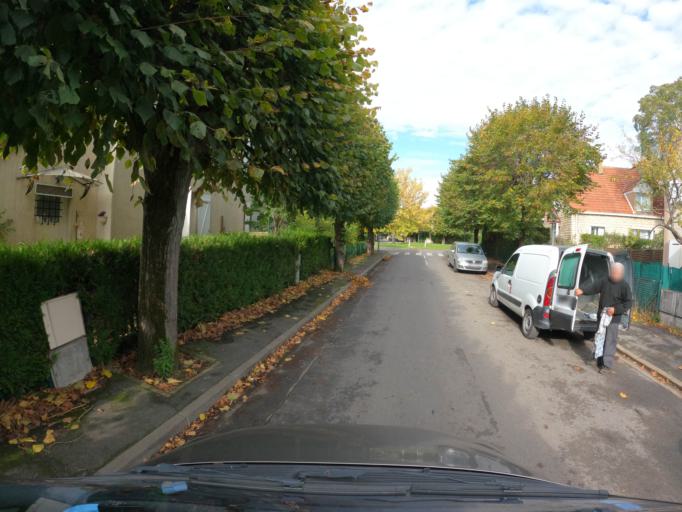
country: FR
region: Ile-de-France
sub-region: Departement de Seine-et-Marne
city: Brou-sur-Chantereine
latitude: 48.8826
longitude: 2.6223
